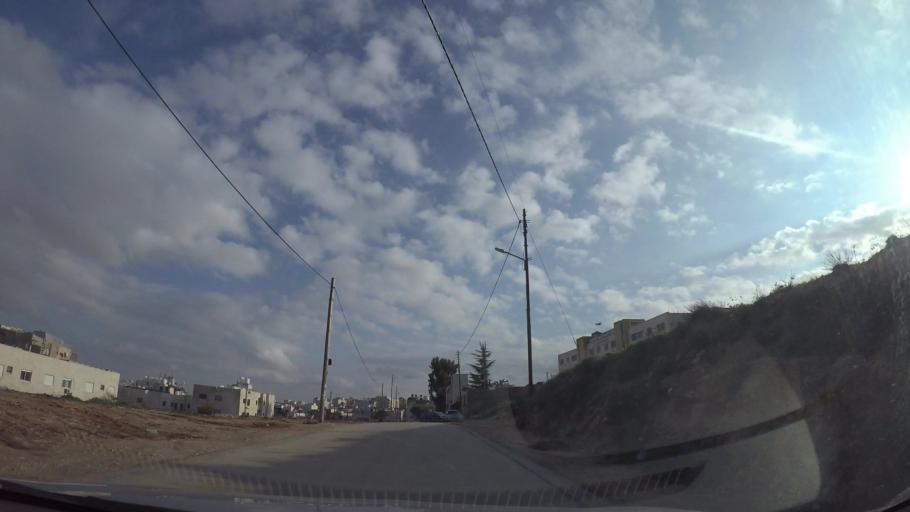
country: JO
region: Amman
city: Al Jubayhah
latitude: 32.0075
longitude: 35.8707
